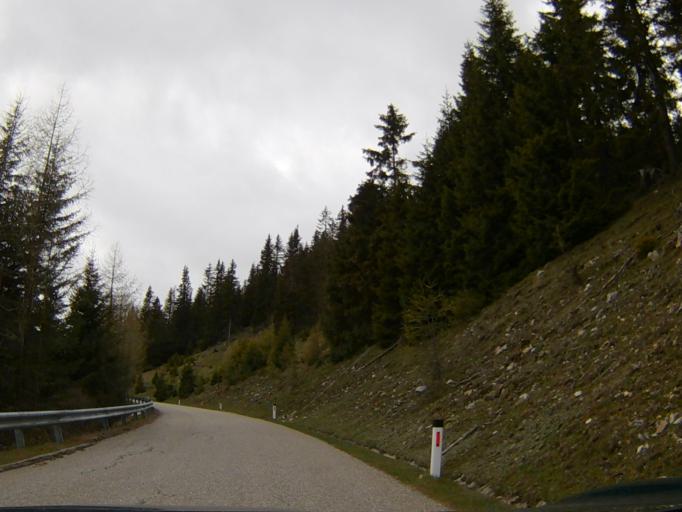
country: AT
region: Carinthia
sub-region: Politischer Bezirk Villach Land
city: Stockenboi
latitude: 46.7510
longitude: 13.4918
